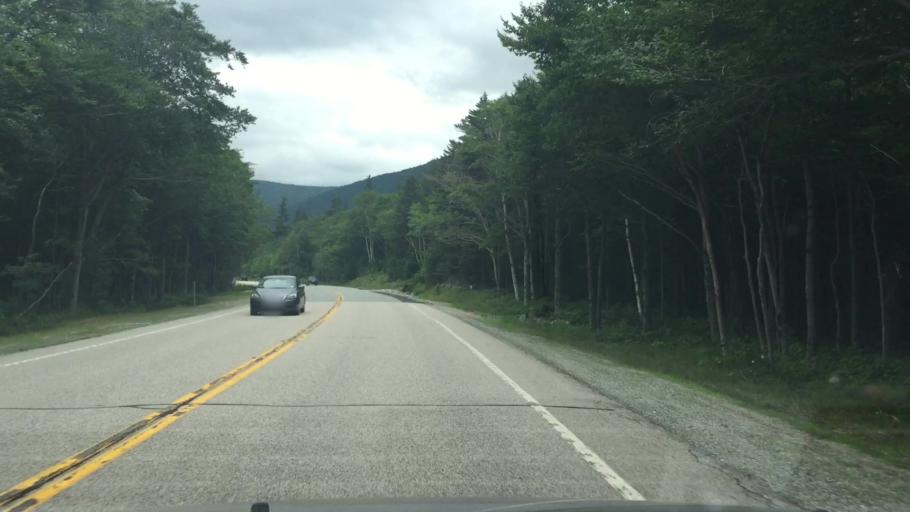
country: US
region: New Hampshire
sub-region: Grafton County
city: Deerfield
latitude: 44.1938
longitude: -71.4062
